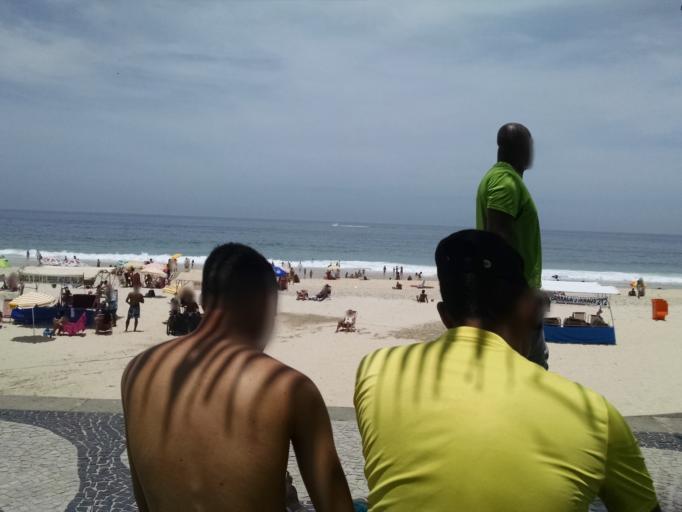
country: BR
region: Rio de Janeiro
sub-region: Rio De Janeiro
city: Rio de Janeiro
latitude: -22.9989
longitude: -43.2596
